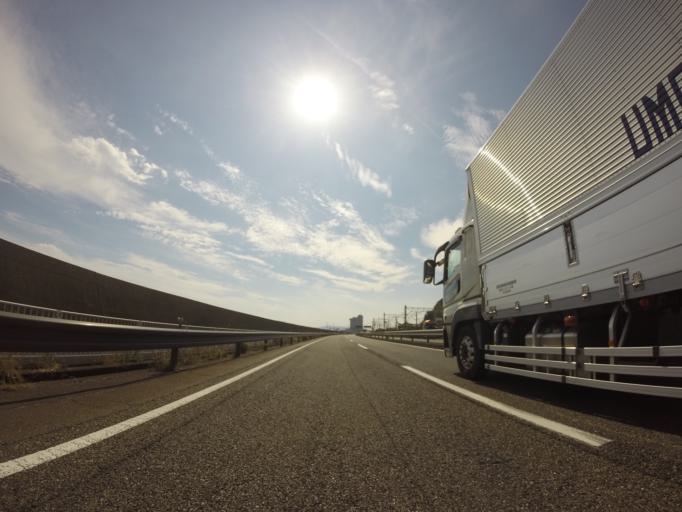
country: JP
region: Shizuoka
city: Fujinomiya
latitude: 35.0631
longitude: 138.5390
